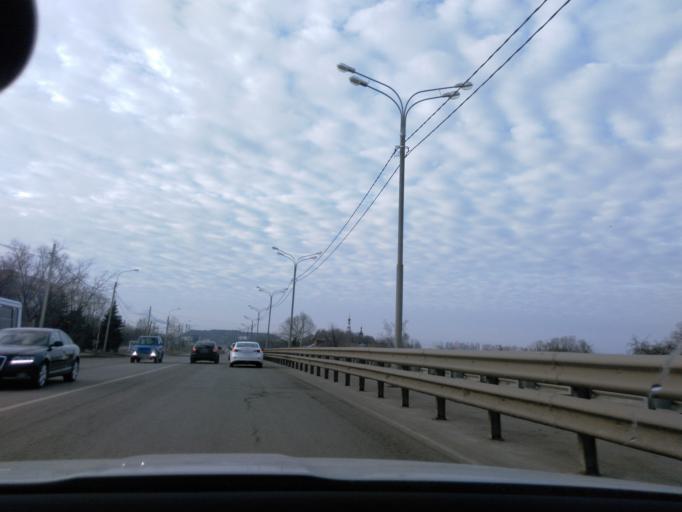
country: RU
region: Moskovskaya
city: Dolgoprudnyy
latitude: 55.9235
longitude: 37.4930
